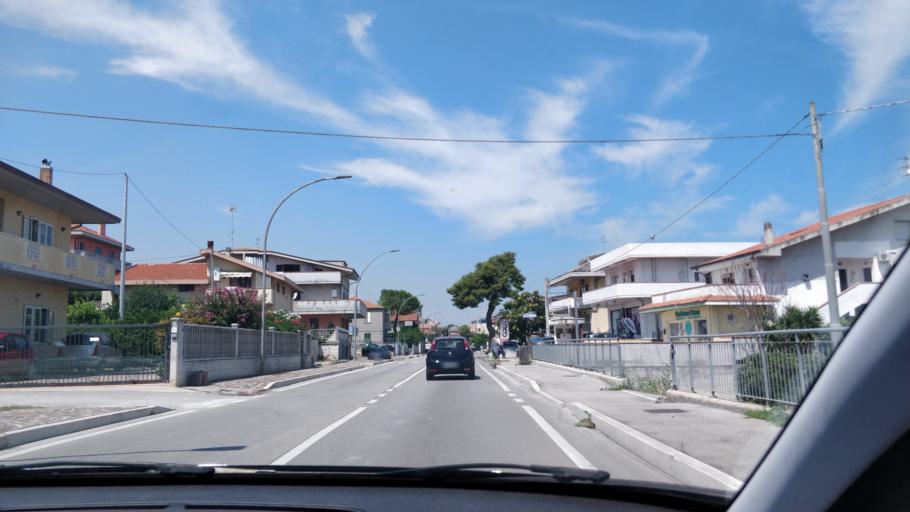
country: IT
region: Abruzzo
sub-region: Provincia di Chieti
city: Francavilla al Mare
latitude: 42.4113
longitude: 14.3036
